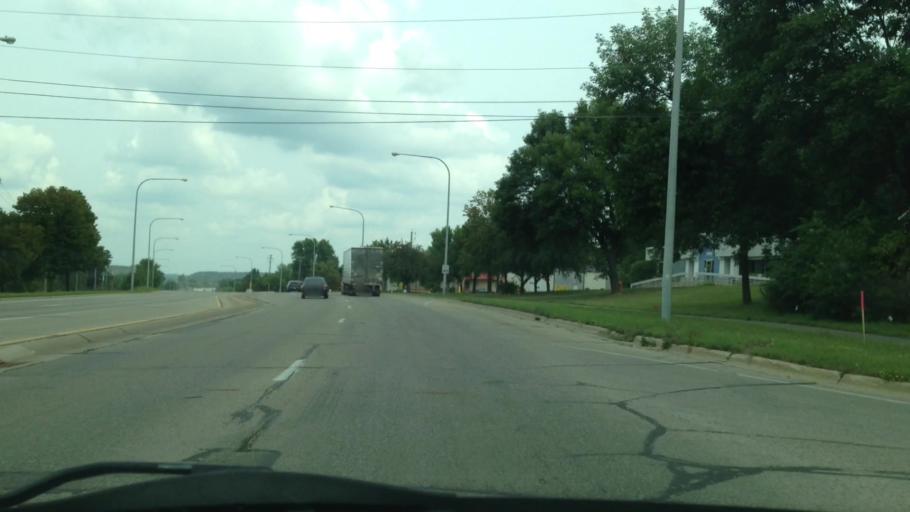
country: US
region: Minnesota
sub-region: Olmsted County
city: Rochester
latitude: 44.0476
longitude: -92.4562
